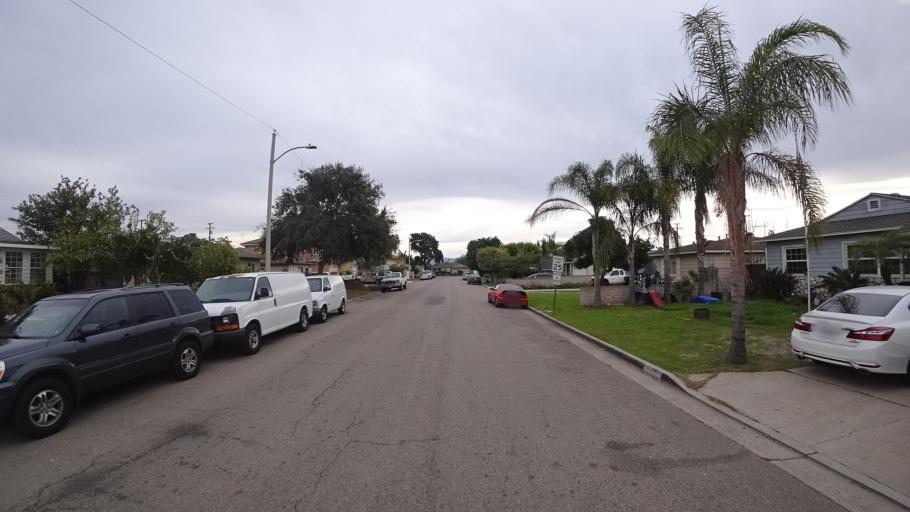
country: US
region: California
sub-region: Orange County
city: Garden Grove
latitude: 33.7792
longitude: -117.9310
